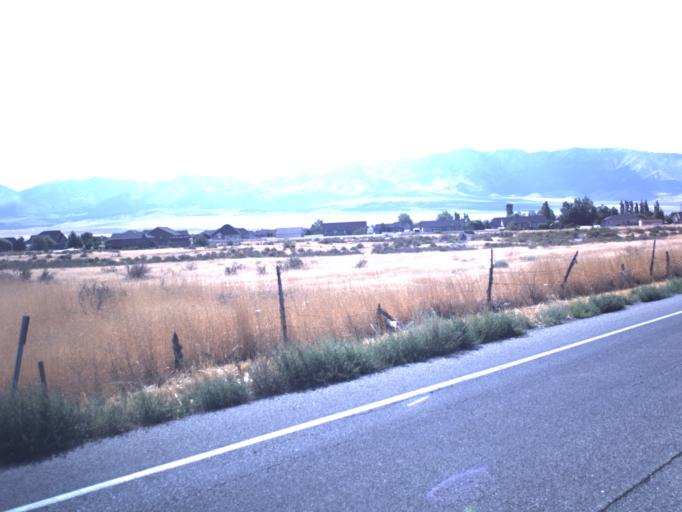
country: US
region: Utah
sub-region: Tooele County
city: Grantsville
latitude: 40.5899
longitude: -112.4186
